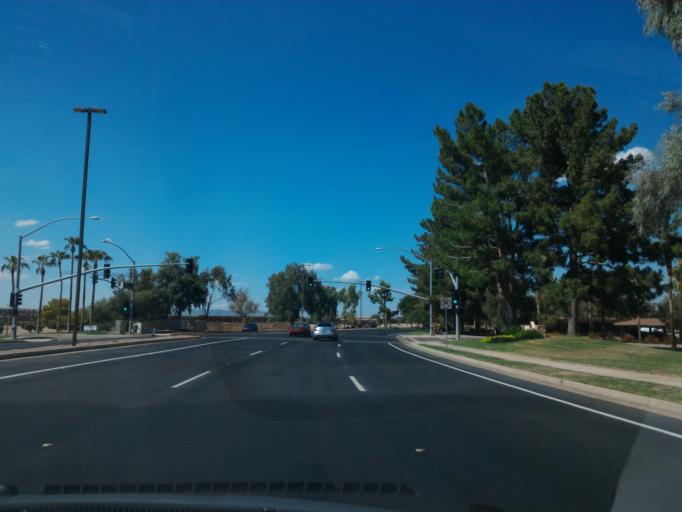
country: US
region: Arizona
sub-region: Maricopa County
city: Sun Lakes
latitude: 33.2574
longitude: -111.8875
